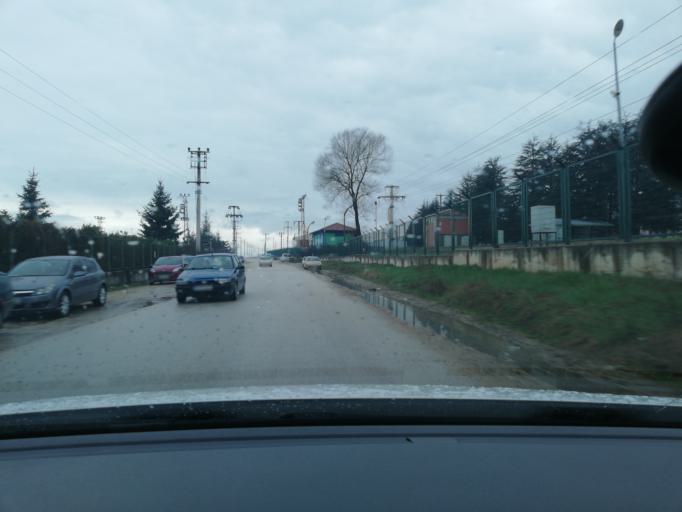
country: TR
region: Bolu
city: Bolu
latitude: 40.7602
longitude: 31.6448
